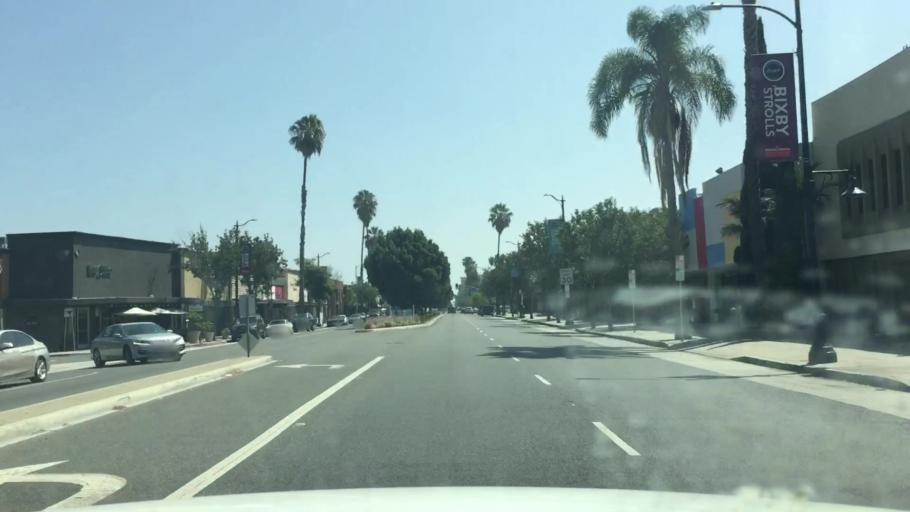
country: US
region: California
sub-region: Los Angeles County
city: Signal Hill
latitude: 33.8362
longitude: -118.1851
